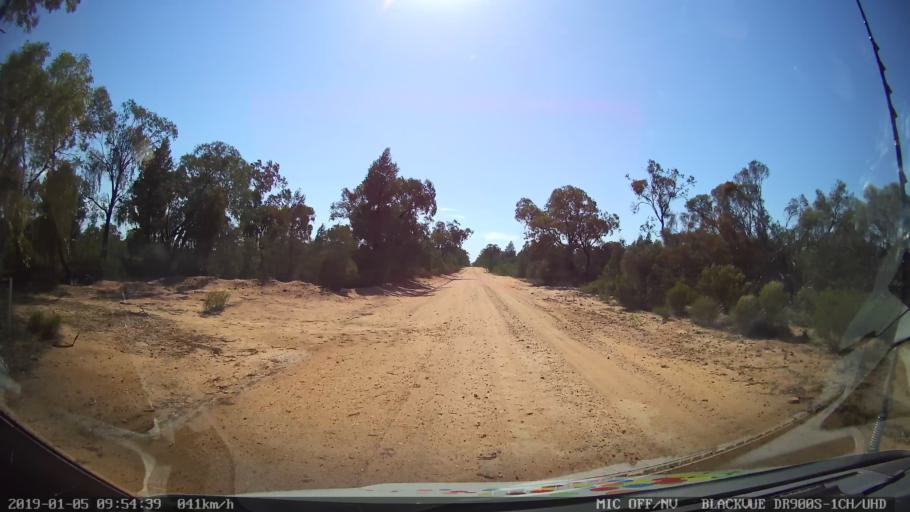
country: AU
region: New South Wales
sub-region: Gilgandra
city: Gilgandra
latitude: -31.6632
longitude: 148.7817
